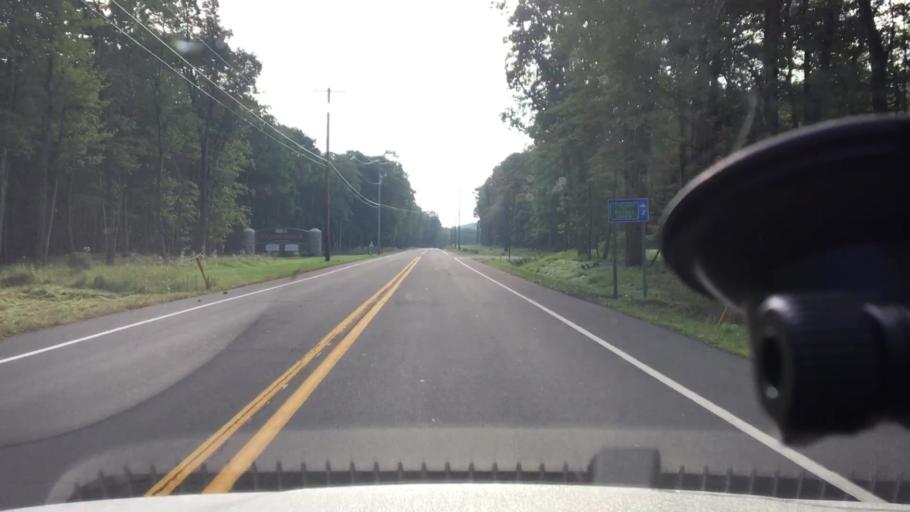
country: US
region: Pennsylvania
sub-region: Monroe County
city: Mount Pocono
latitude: 41.1046
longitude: -75.3777
